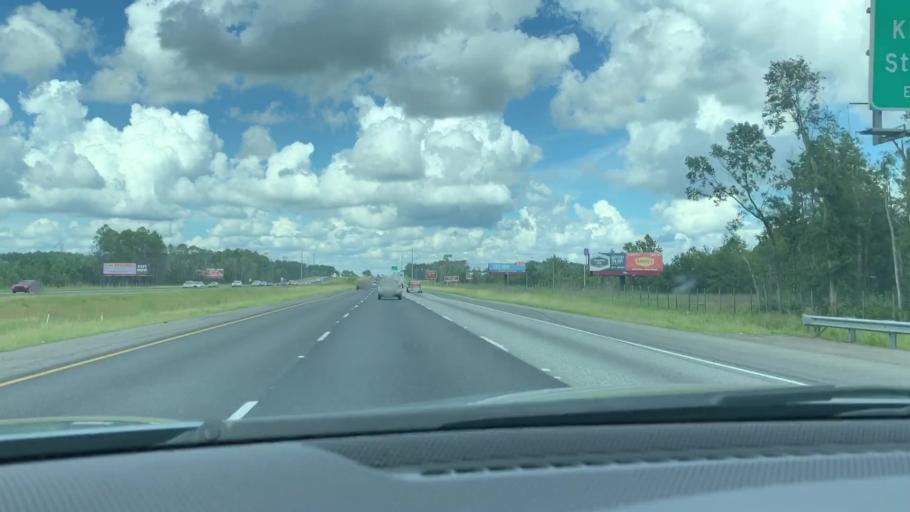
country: US
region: Georgia
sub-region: Camden County
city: Kingsland
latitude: 30.7828
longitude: -81.6570
